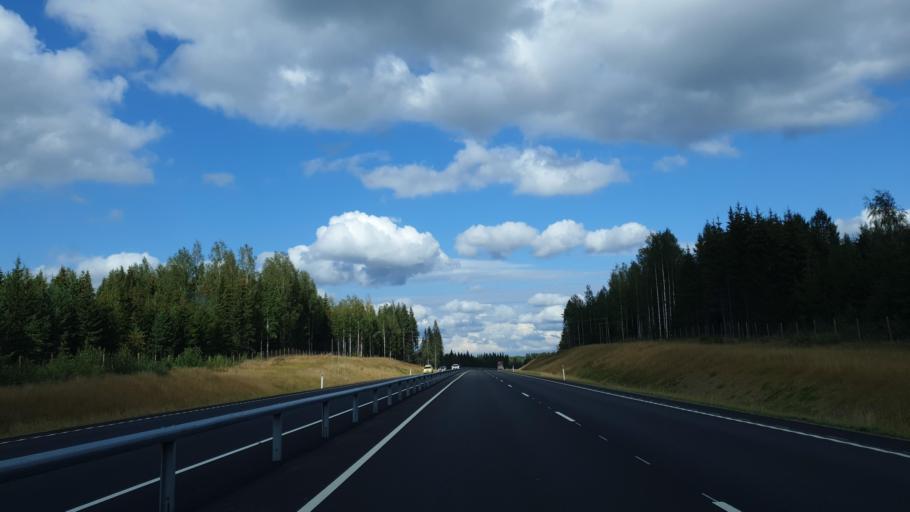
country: FI
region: Southern Savonia
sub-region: Mikkeli
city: Mikkeli
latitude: 61.7267
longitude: 27.3706
